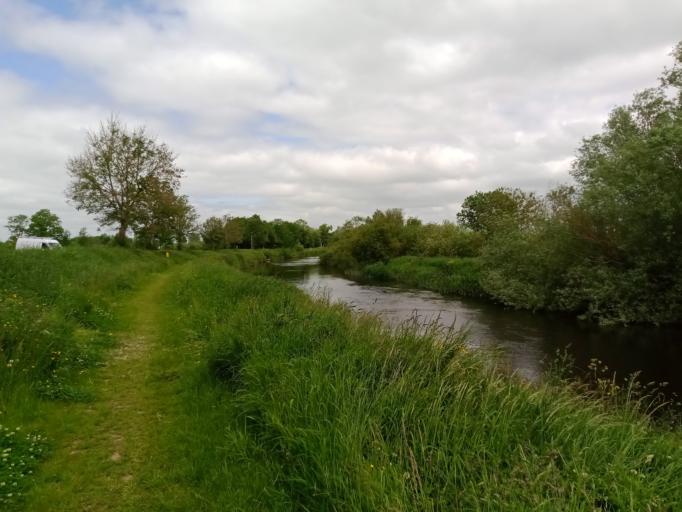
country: IE
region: Leinster
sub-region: County Carlow
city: Carlow
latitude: 52.8069
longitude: -6.9671
